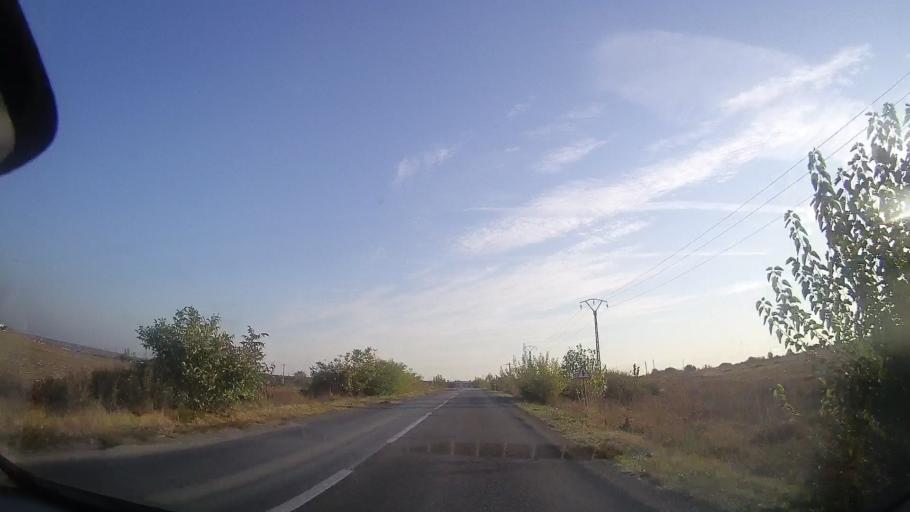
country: RO
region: Timis
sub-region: Comuna Pischia
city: Pischia
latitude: 45.8872
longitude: 21.3471
